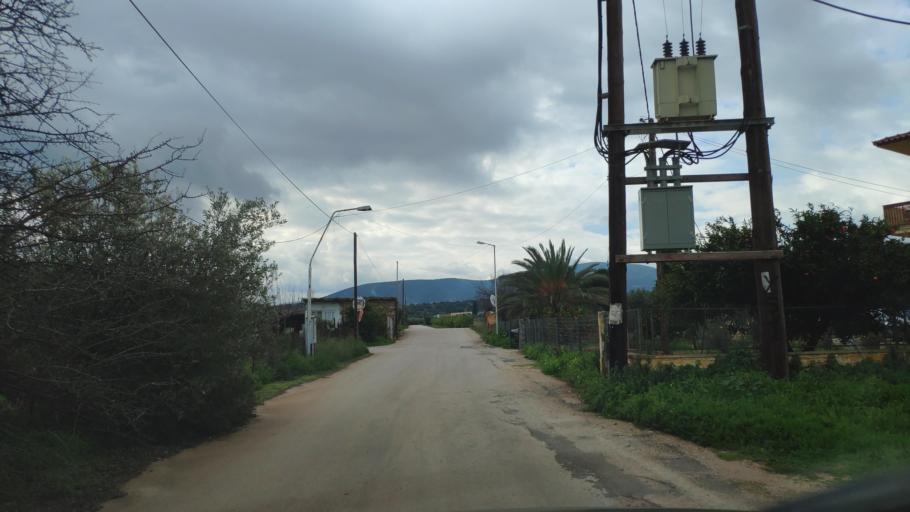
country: GR
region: Peloponnese
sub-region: Nomos Argolidos
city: Nea Kios
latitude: 37.5416
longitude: 22.7094
